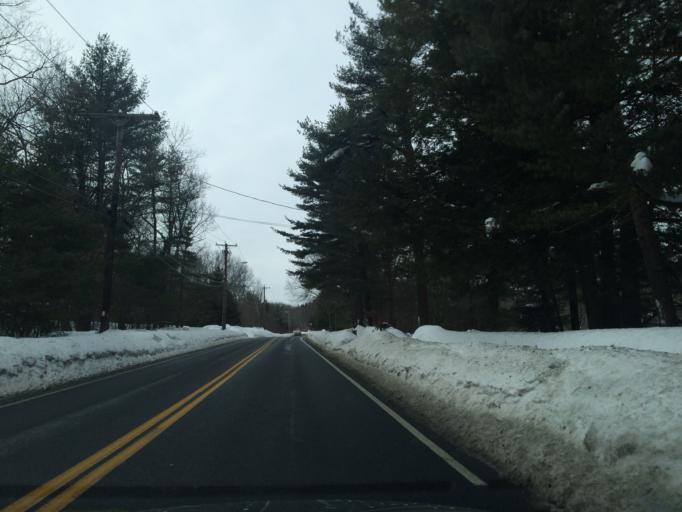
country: US
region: Massachusetts
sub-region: Middlesex County
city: Weston
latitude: 42.3553
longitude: -71.3020
